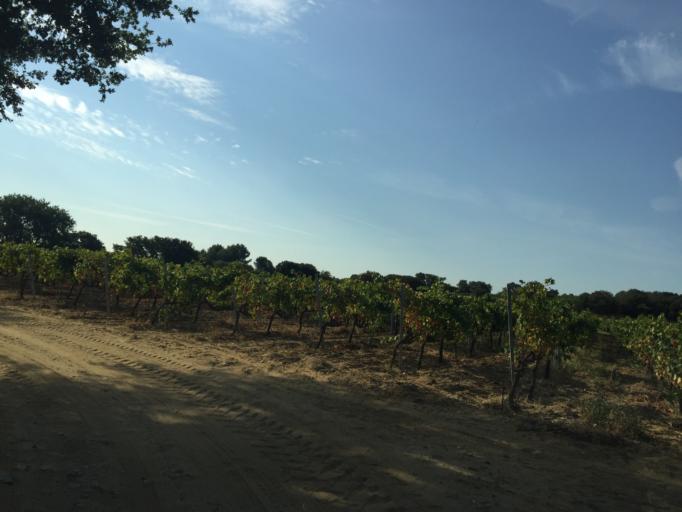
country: FR
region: Provence-Alpes-Cote d'Azur
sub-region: Departement du Vaucluse
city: Courthezon
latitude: 44.0788
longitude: 4.8593
